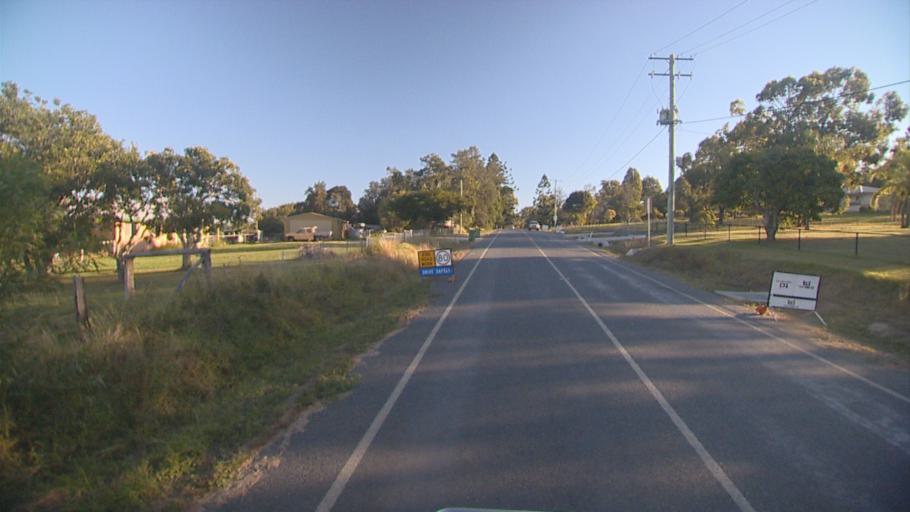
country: AU
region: Queensland
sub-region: Logan
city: Logan Reserve
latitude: -27.7182
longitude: 153.1134
